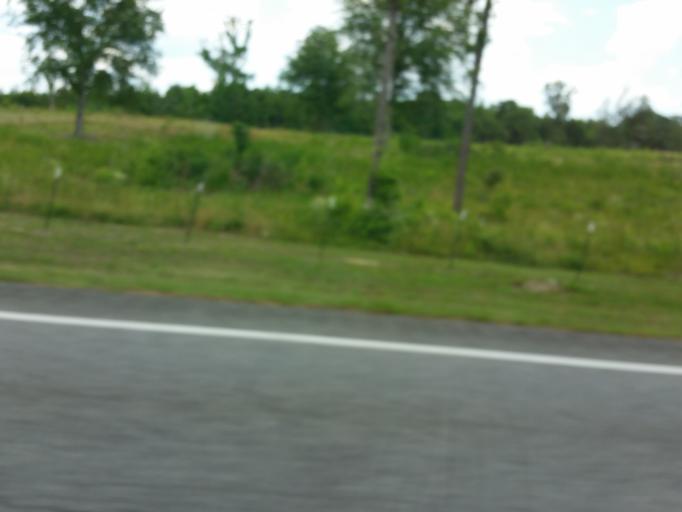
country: US
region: Alabama
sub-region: Sumter County
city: York
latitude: 32.3938
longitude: -88.2054
